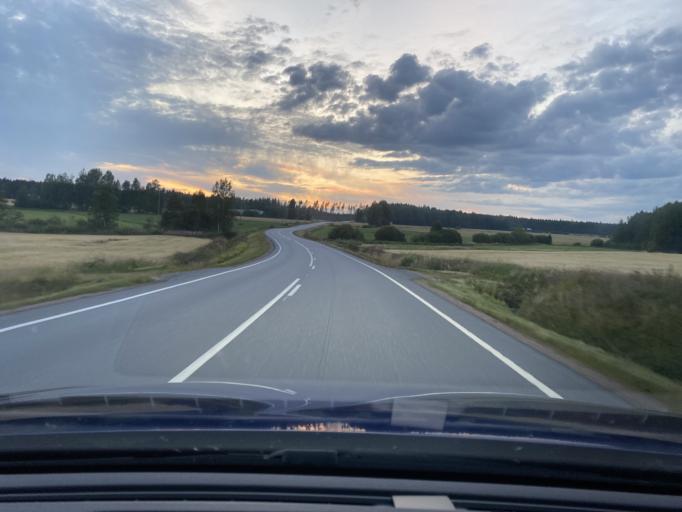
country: FI
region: Southern Ostrobothnia
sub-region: Suupohja
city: Kauhajoki
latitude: 62.2223
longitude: 22.2817
